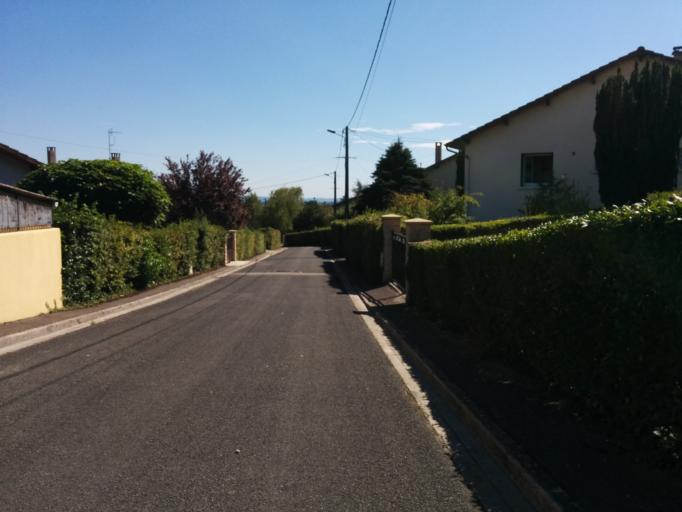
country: FR
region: Rhone-Alpes
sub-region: Departement de l'Ain
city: Meximieux
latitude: 45.9052
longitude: 5.1881
